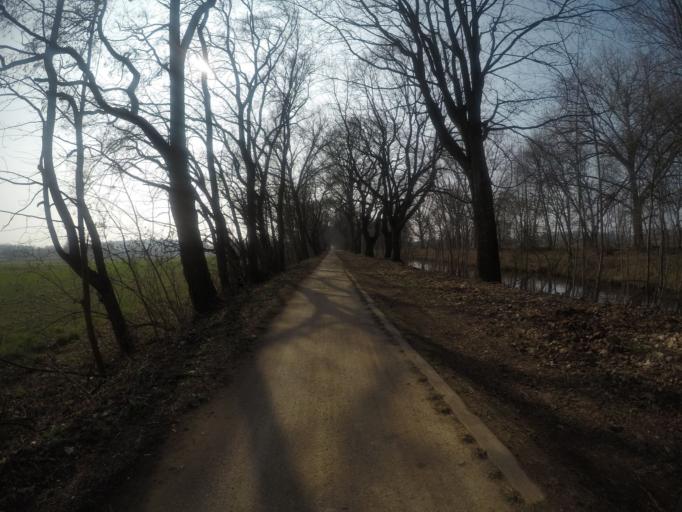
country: DE
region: Brandenburg
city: Mittenwalde
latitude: 52.2653
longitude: 13.5522
